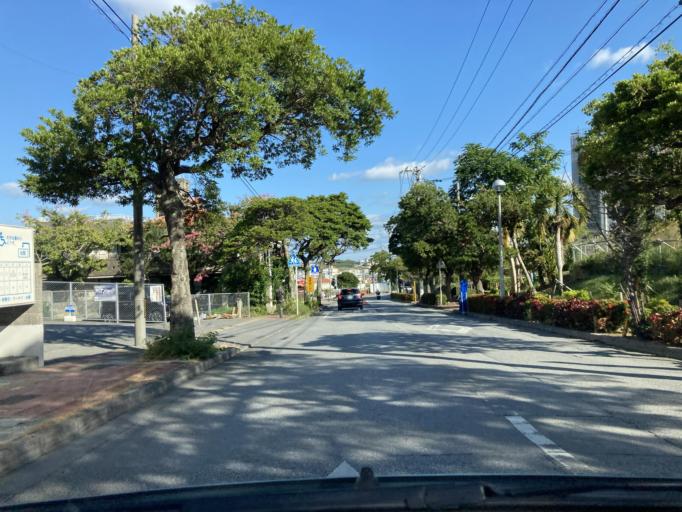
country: JP
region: Okinawa
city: Ginowan
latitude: 26.2270
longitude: 127.7326
